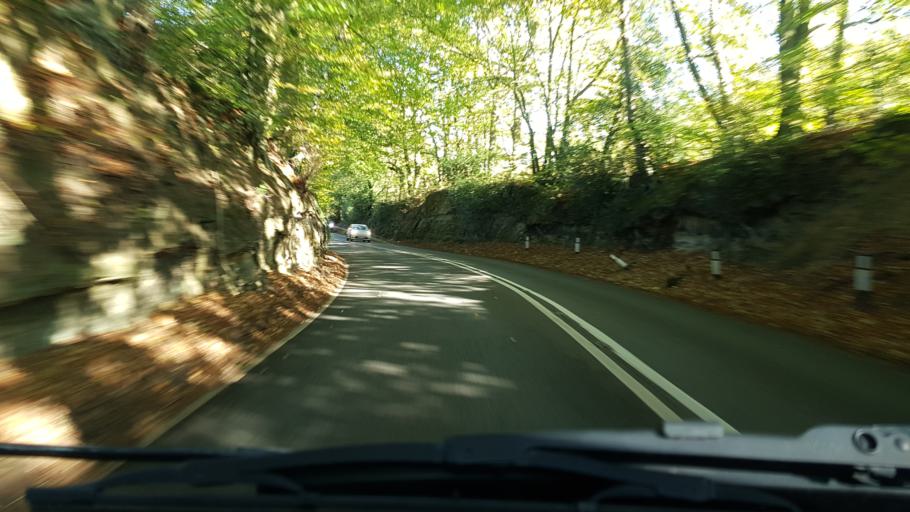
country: GB
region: England
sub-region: Surrey
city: Dorking
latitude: 51.2208
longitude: -0.3850
